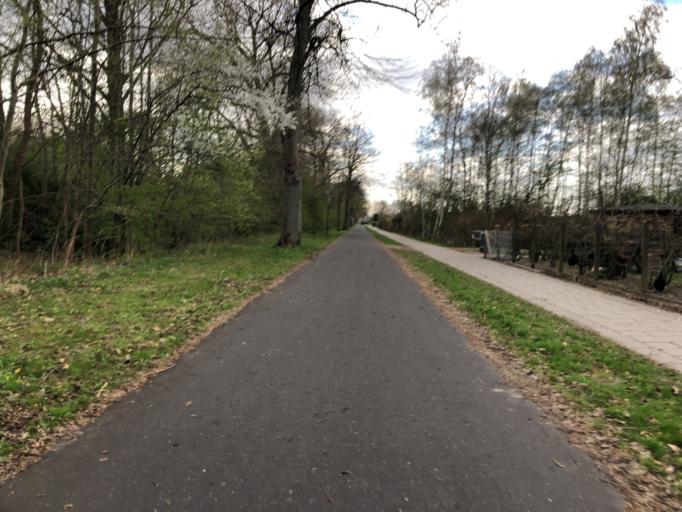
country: DK
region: Zealand
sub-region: Ringsted Kommune
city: Ringsted
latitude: 55.4481
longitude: 11.8093
